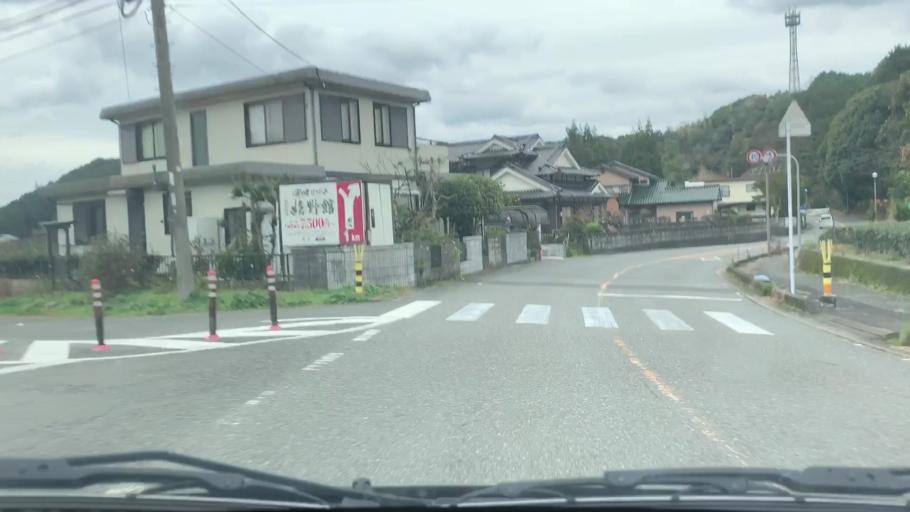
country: JP
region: Saga Prefecture
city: Ureshinomachi-shimojuku
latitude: 33.1061
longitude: 129.9775
